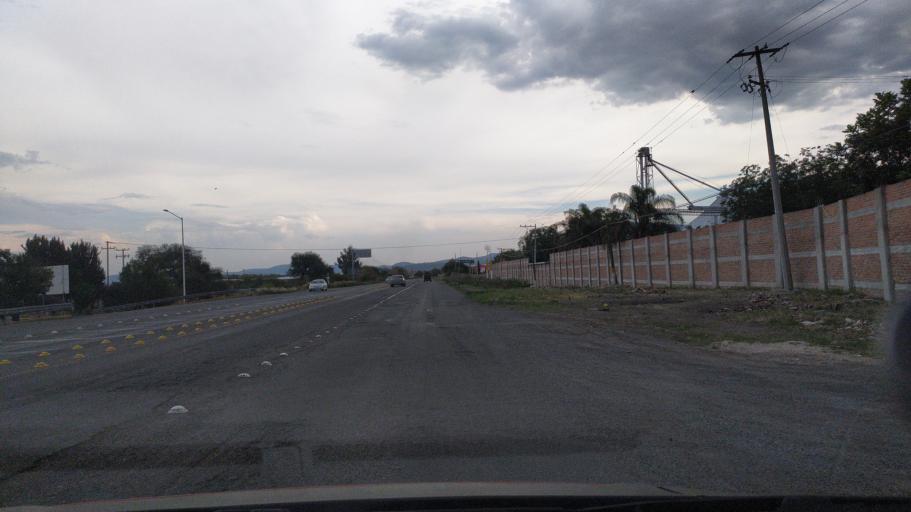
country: MX
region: Guanajuato
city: Ciudad Manuel Doblado
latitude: 20.7408
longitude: -101.9317
